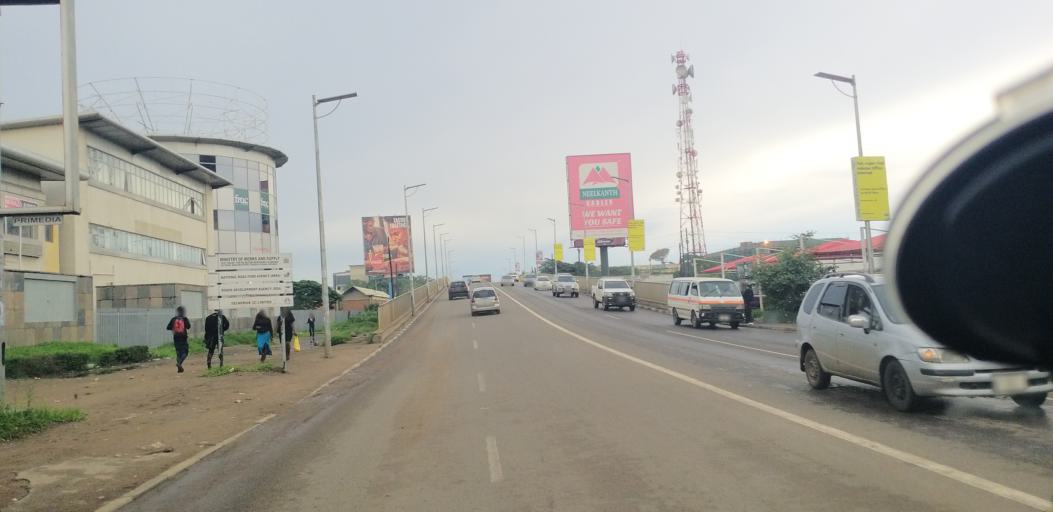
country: ZM
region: Lusaka
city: Lusaka
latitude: -15.4161
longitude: 28.2819
